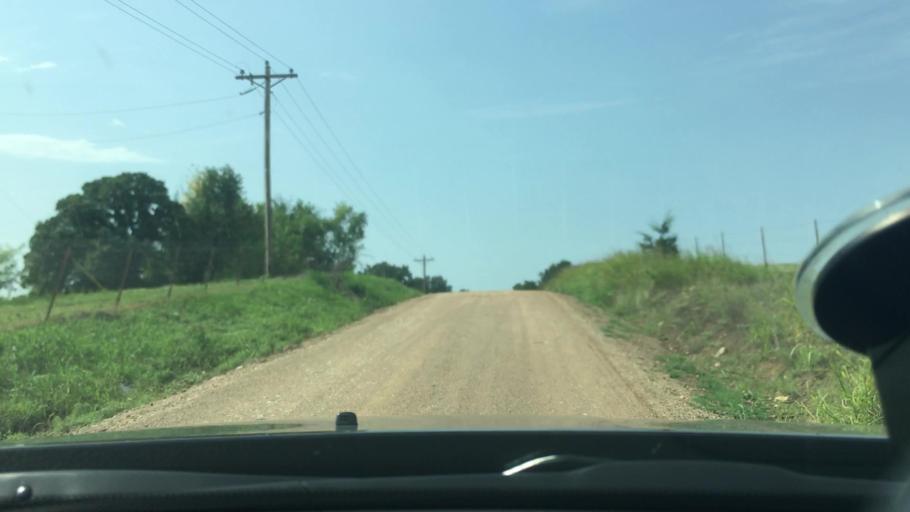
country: US
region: Oklahoma
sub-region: Atoka County
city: Atoka
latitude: 34.4591
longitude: -96.0407
